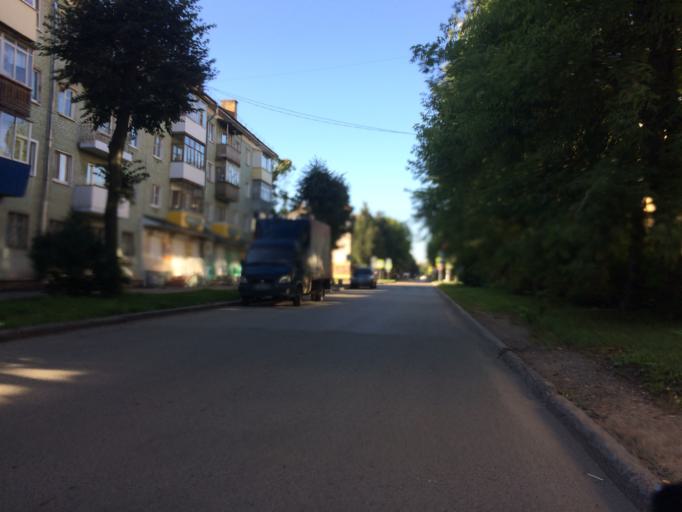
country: RU
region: Mariy-El
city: Yoshkar-Ola
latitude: 56.6389
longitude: 47.8827
